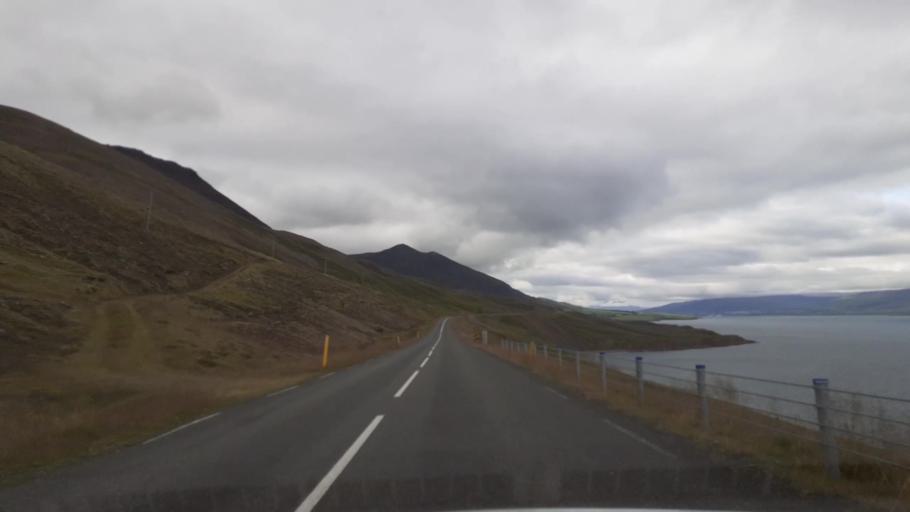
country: IS
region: Northeast
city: Akureyri
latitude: 65.8465
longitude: -18.0588
